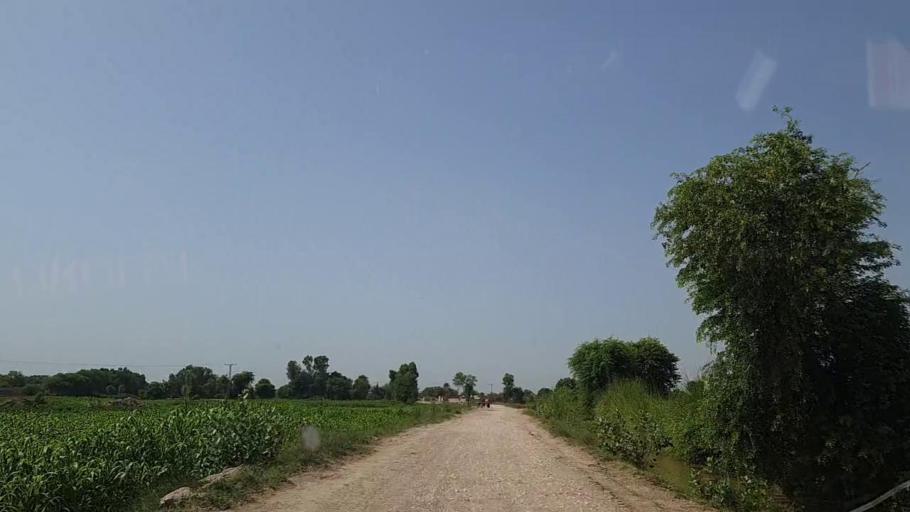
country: PK
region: Sindh
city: Naushahro Firoz
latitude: 26.8550
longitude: 68.0284
